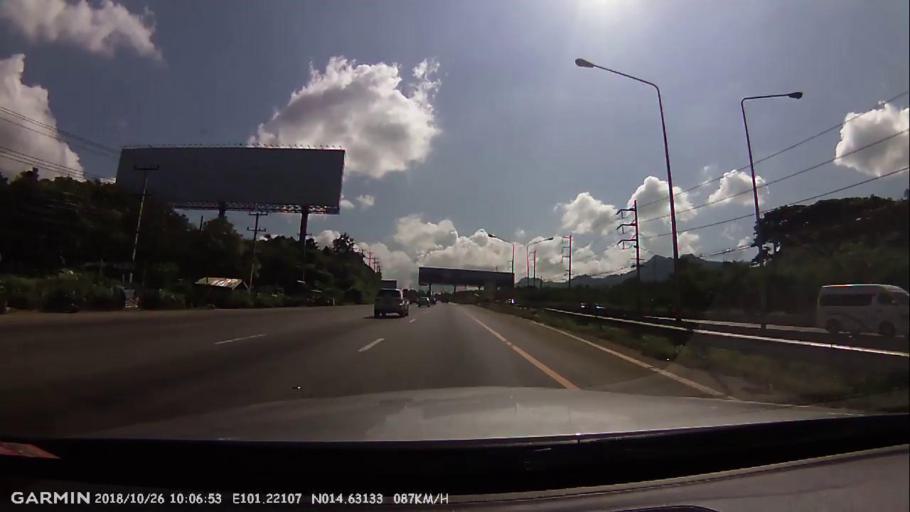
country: TH
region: Sara Buri
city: Muak Lek
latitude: 14.6313
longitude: 101.2212
